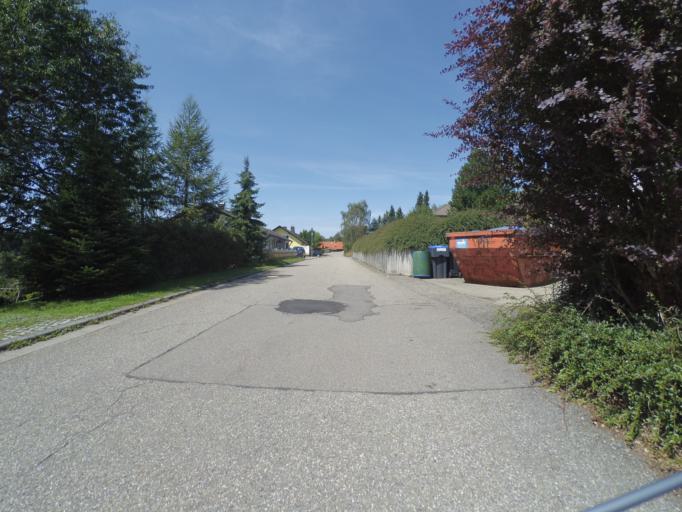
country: DE
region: Baden-Wuerttemberg
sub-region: Freiburg Region
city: Lenzkirch
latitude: 47.8699
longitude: 8.2369
